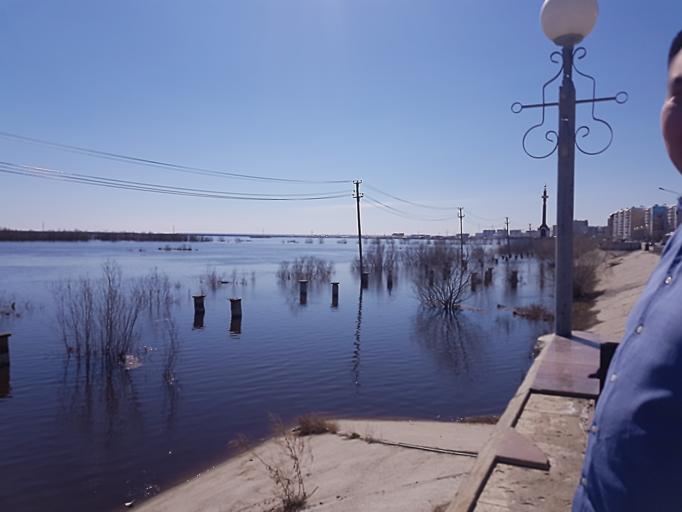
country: RU
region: Sakha
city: Yakutsk
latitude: 62.0255
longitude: 129.7439
